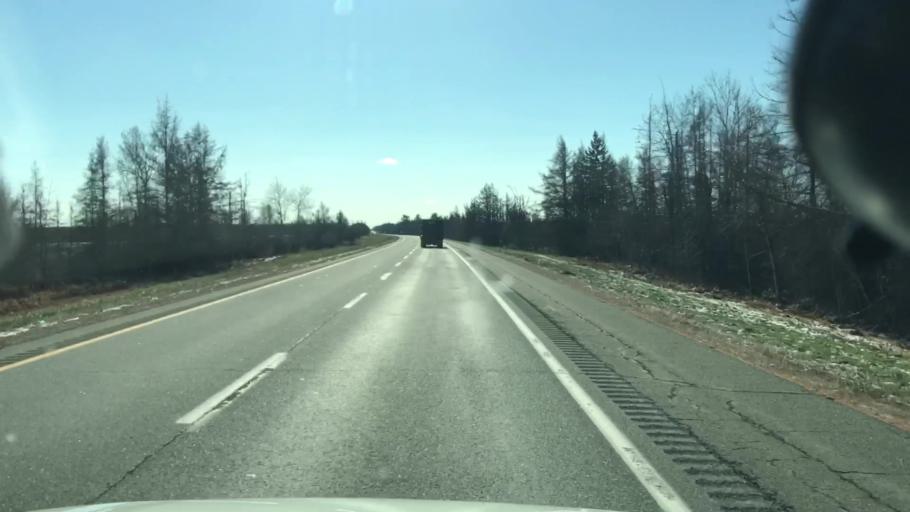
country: US
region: Maine
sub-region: Penobscot County
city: Greenbush
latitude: 45.0160
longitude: -68.6994
